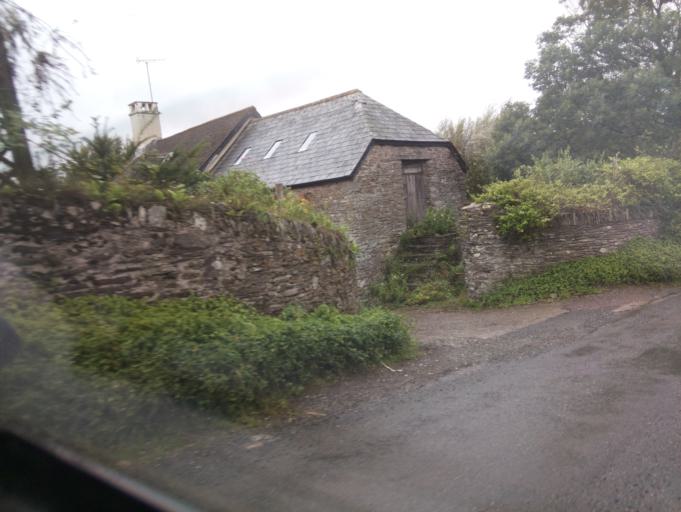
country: GB
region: England
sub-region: Devon
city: Dartmouth
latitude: 50.3464
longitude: -3.6389
